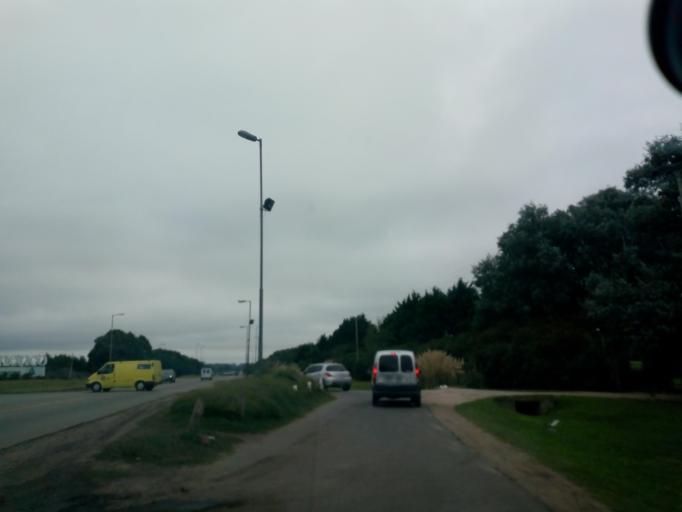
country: AR
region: Buenos Aires
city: Mar del Plata
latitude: -38.0788
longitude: -57.5831
